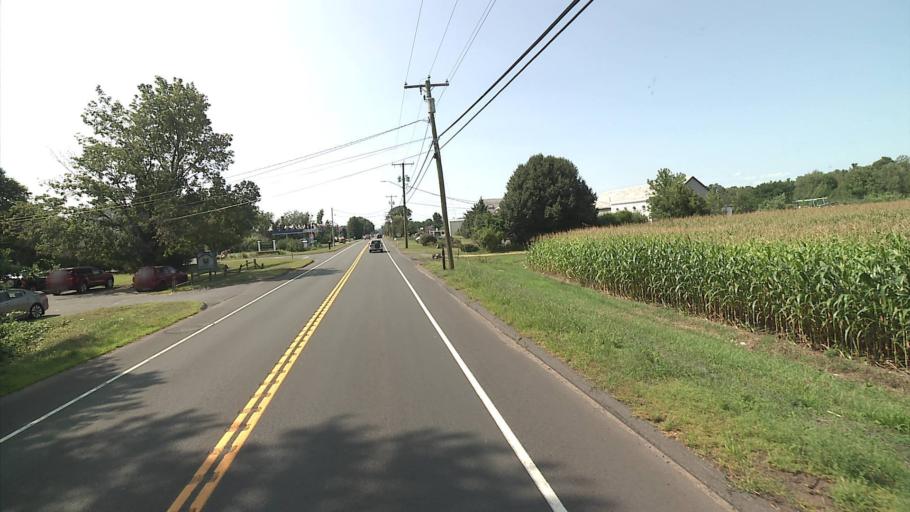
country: US
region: Connecticut
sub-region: Hartford County
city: South Windsor
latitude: 41.8507
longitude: -72.5779
